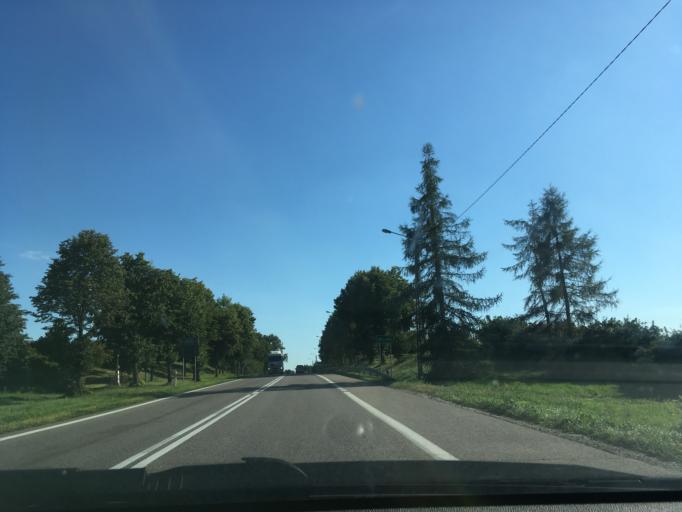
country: PL
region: Podlasie
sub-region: Powiat sokolski
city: Suchowola
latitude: 53.4879
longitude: 23.0943
